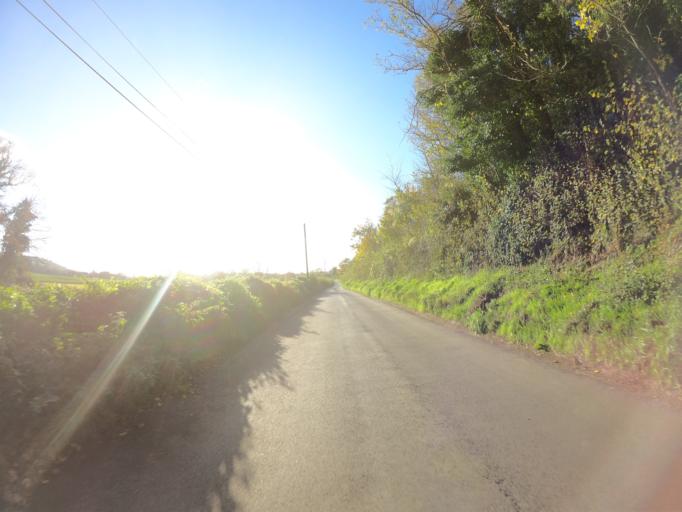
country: GB
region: England
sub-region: Kent
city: Eynsford
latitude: 51.3686
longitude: 0.2022
